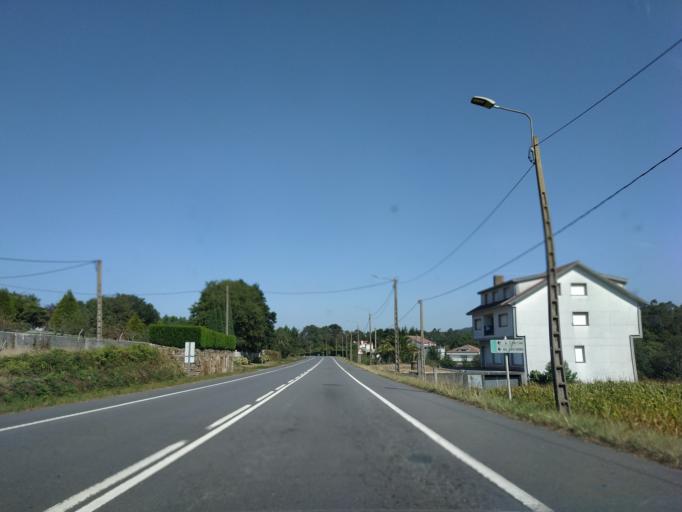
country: ES
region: Galicia
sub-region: Provincia da Coruna
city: Carballo
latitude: 43.2329
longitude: -8.6509
